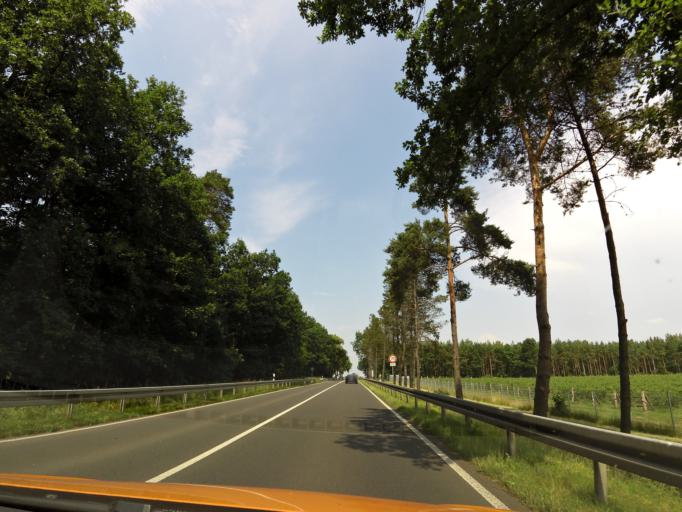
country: DE
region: Brandenburg
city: Pritzwalk
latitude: 53.1774
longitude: 12.1899
